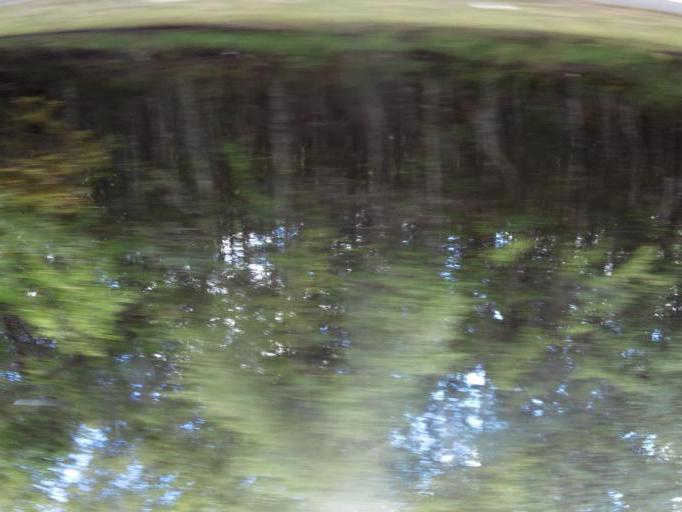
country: US
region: Georgia
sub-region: Charlton County
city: Folkston
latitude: 31.0032
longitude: -82.0269
